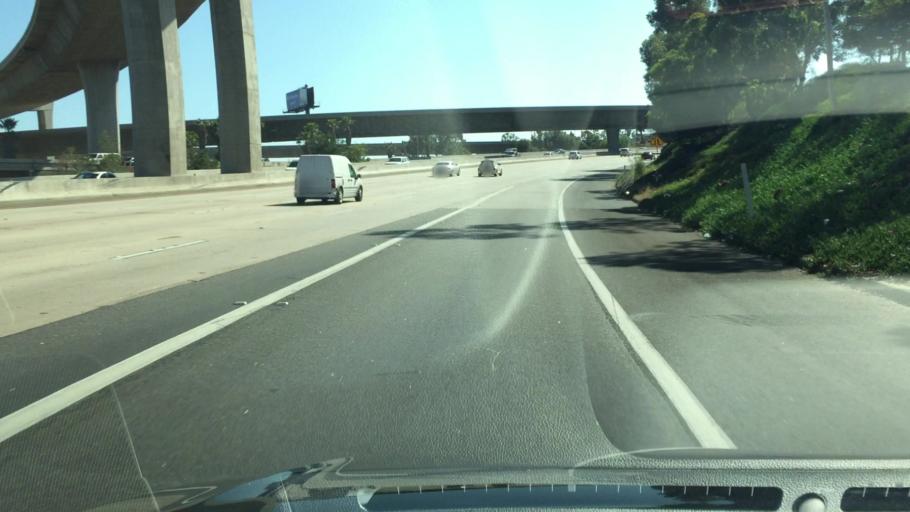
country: US
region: California
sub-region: San Diego County
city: Lemon Grove
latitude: 32.7484
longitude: -117.0180
